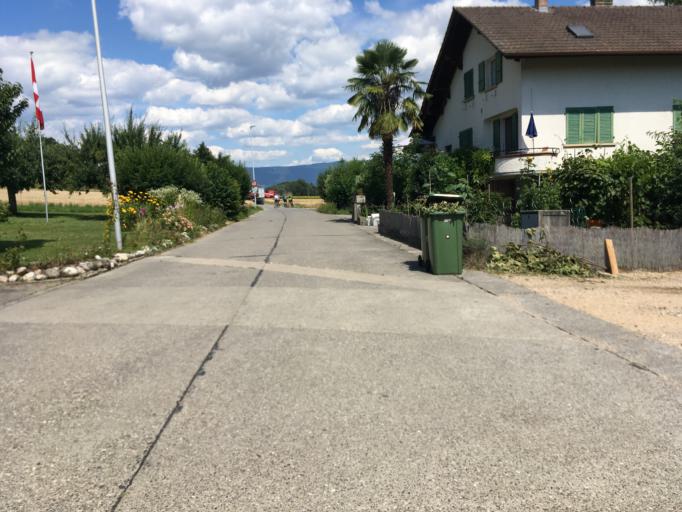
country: CH
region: Fribourg
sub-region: See District
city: Bas-Vully
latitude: 46.9653
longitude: 7.1114
